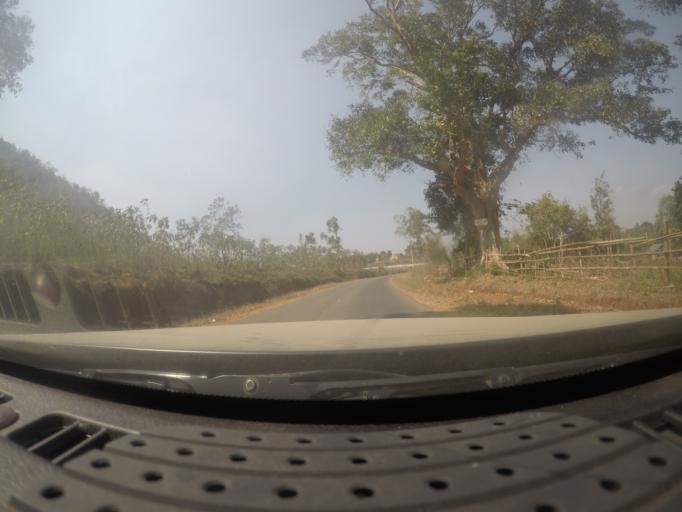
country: MM
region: Mandalay
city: Kyaukse
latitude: 21.1387
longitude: 96.4485
